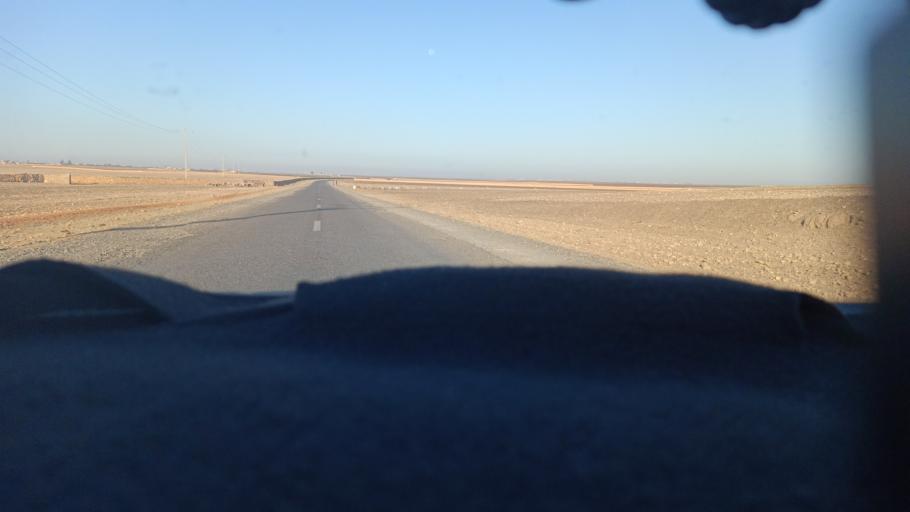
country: MA
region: Doukkala-Abda
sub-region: Safi
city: Youssoufia
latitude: 32.3713
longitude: -8.6885
